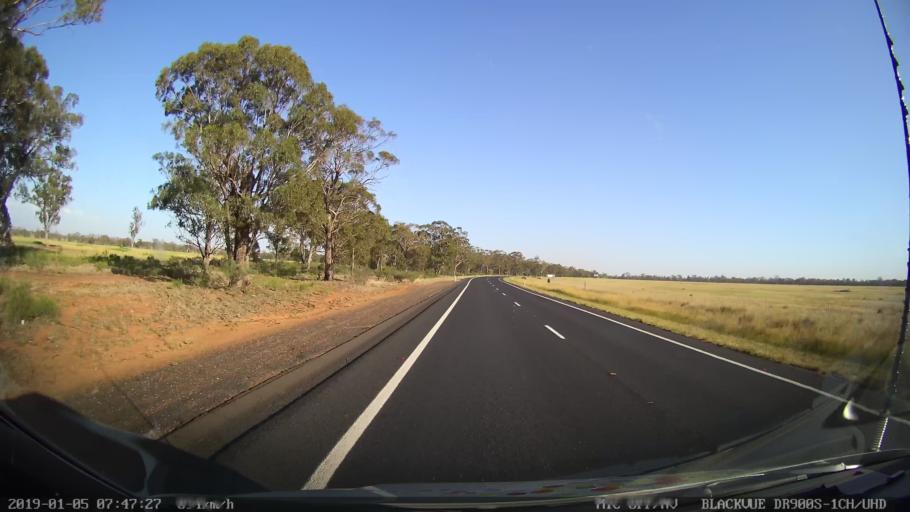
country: AU
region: New South Wales
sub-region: Gilgandra
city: Gilgandra
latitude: -31.8303
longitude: 148.6389
